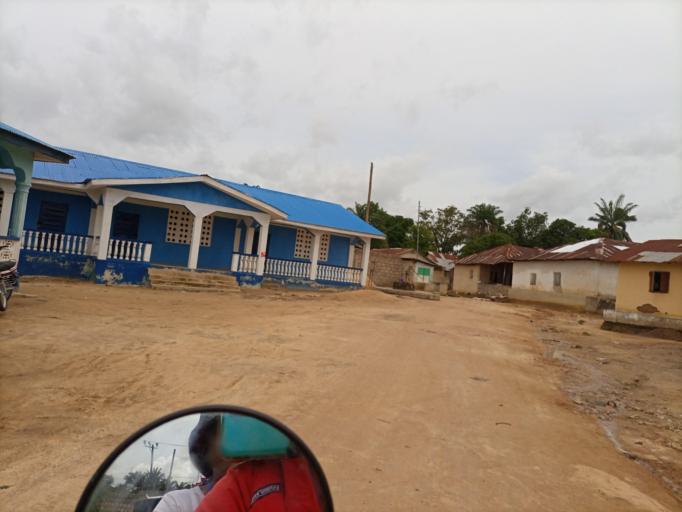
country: SL
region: Southern Province
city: Bo
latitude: 7.9497
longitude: -11.7467
